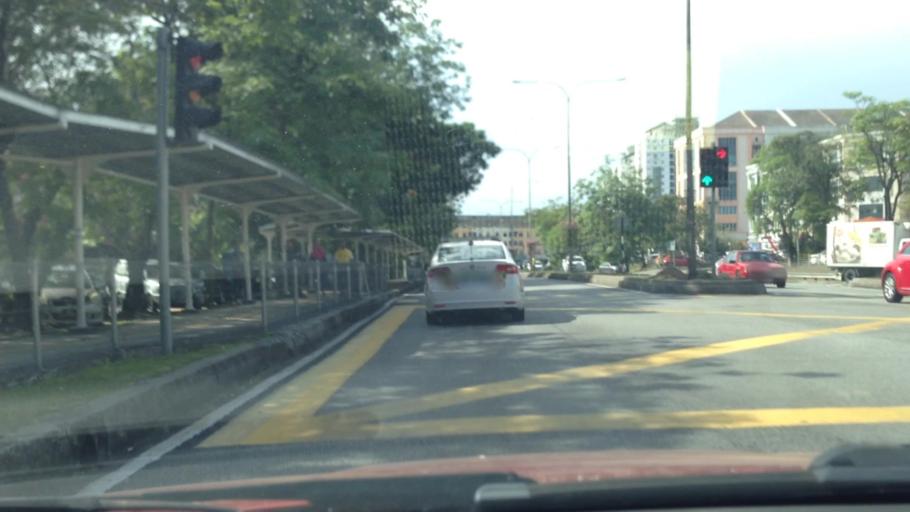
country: MY
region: Selangor
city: Subang Jaya
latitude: 3.0483
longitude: 101.5873
